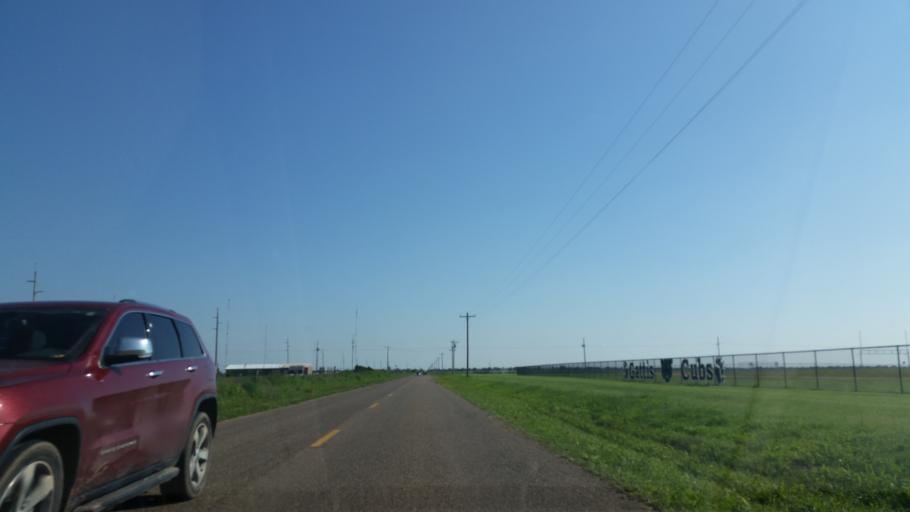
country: US
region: New Mexico
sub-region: Curry County
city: Clovis
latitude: 34.4507
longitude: -103.2140
